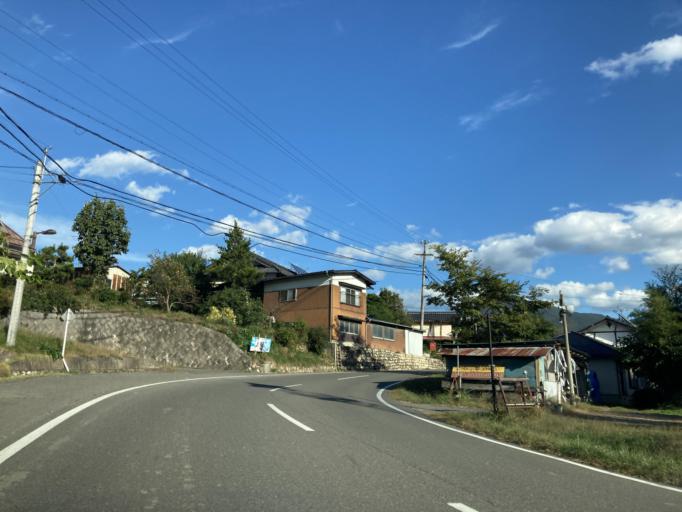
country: JP
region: Nagano
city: Omachi
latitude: 36.4388
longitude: 138.0041
